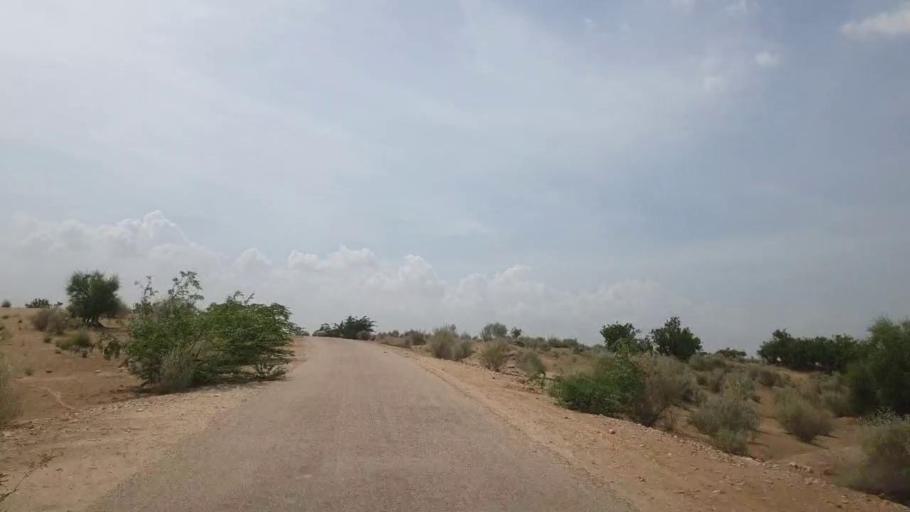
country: PK
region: Sindh
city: Kot Diji
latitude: 27.2358
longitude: 69.0860
